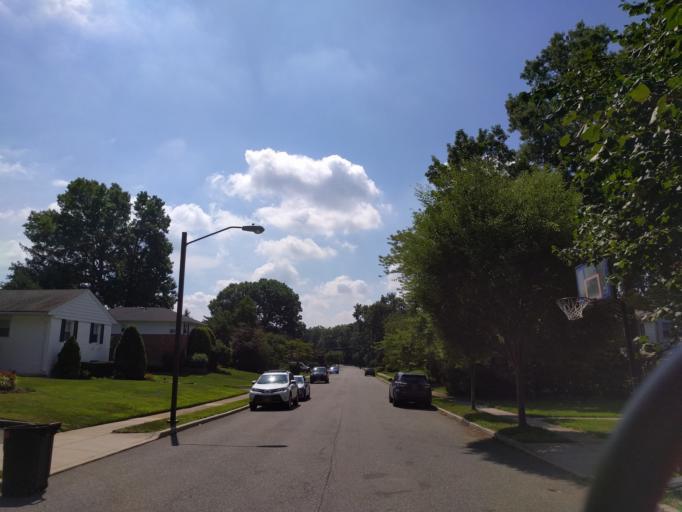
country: US
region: New York
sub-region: Nassau County
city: East Norwich
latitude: 40.8545
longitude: -73.5289
